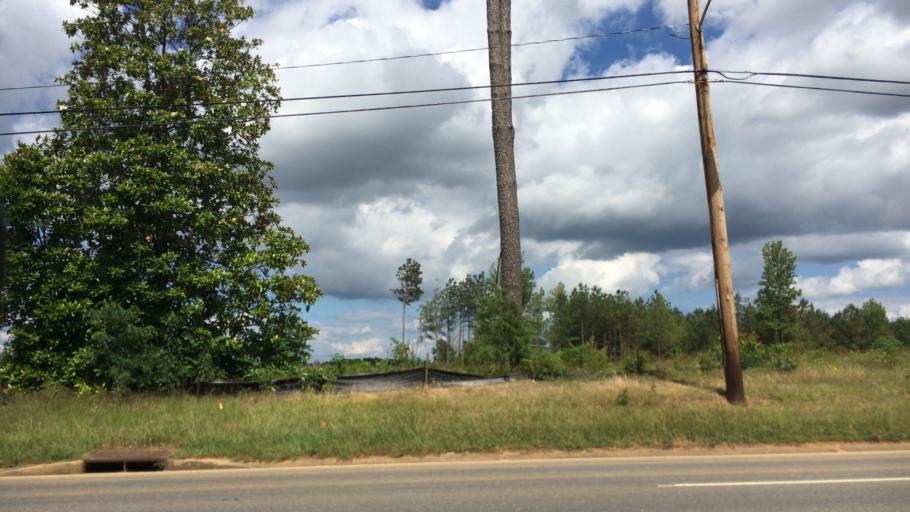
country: US
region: Louisiana
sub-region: Lincoln Parish
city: Ruston
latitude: 32.5075
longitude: -92.6374
